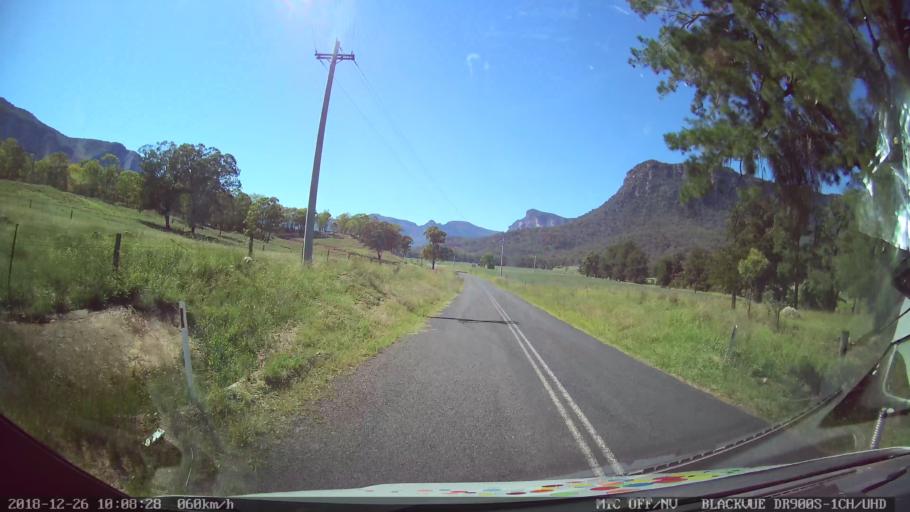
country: AU
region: New South Wales
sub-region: Mid-Western Regional
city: Kandos
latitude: -33.0978
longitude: 150.2305
